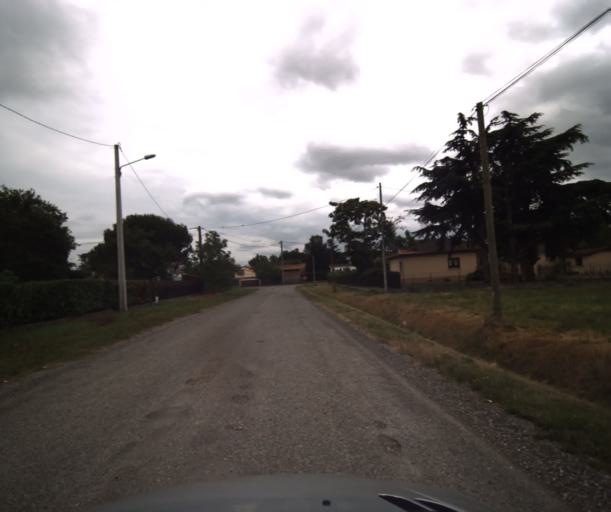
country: FR
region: Midi-Pyrenees
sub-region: Departement de la Haute-Garonne
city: Labarthe-sur-Leze
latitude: 43.4535
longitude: 1.4160
